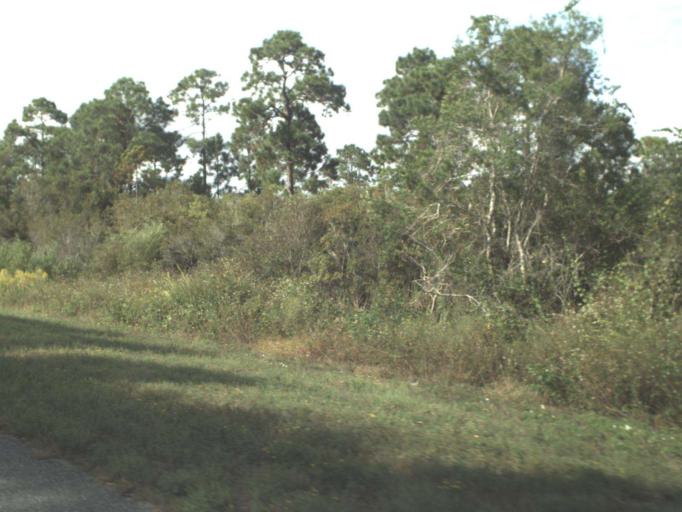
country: US
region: Florida
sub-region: Gulf County
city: Port Saint Joe
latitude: 29.8494
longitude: -85.3298
